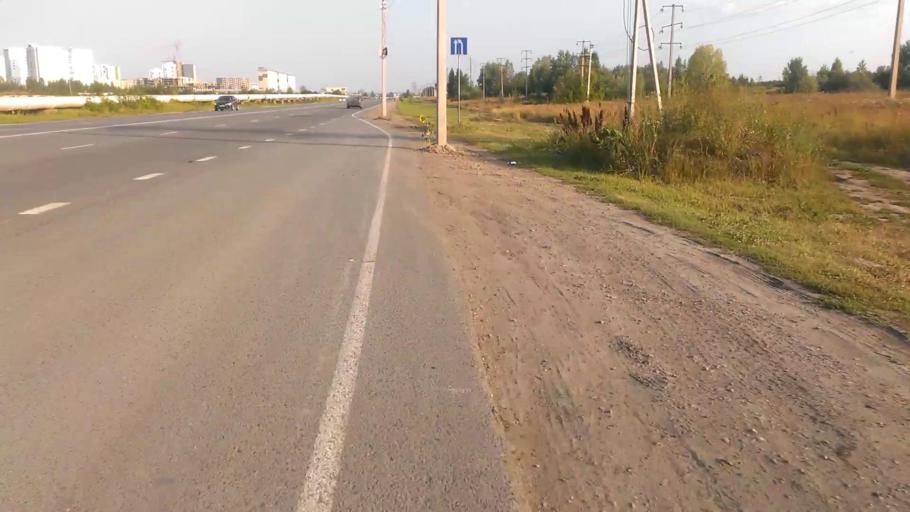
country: RU
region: Altai Krai
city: Novosilikatnyy
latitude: 53.3468
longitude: 83.6319
